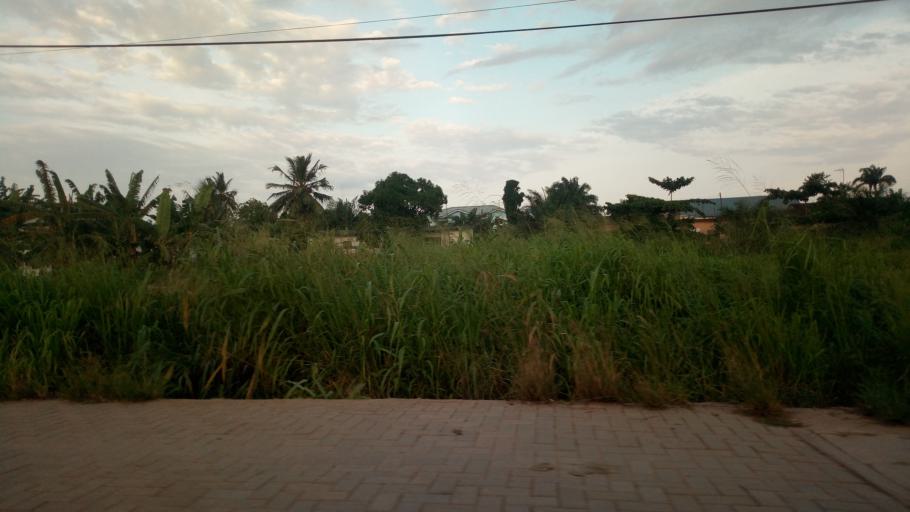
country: GH
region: Western
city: Takoradi
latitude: 4.9314
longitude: -1.7799
